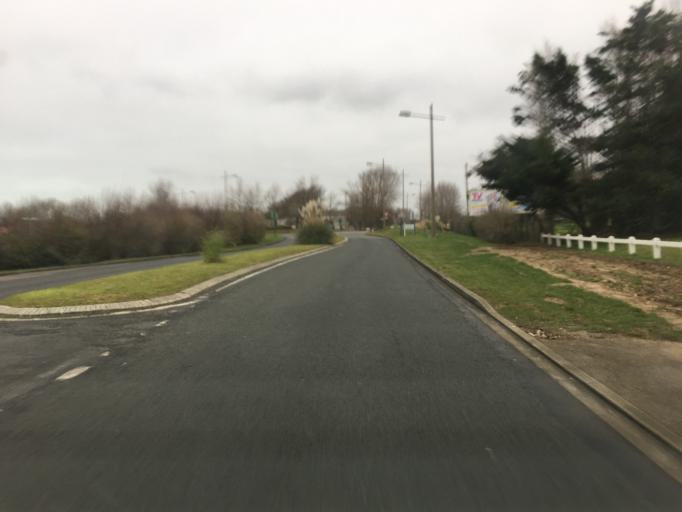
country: FR
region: Nord-Pas-de-Calais
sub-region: Departement du Pas-de-Calais
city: Le Portel
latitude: 50.6971
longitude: 1.5797
